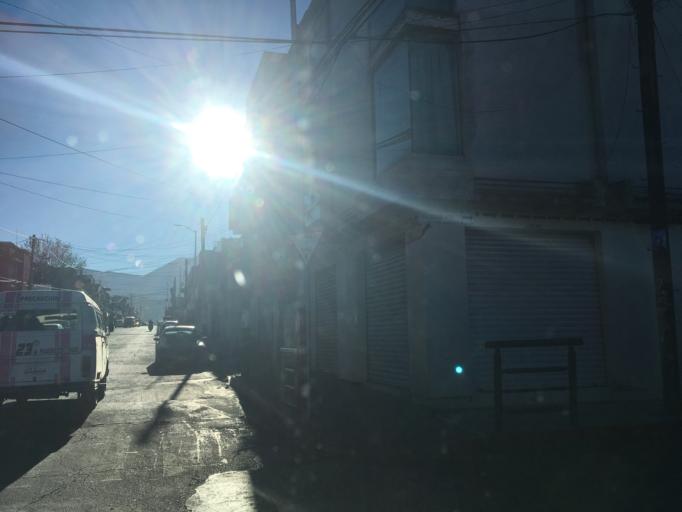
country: MX
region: Michoacan
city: Heroica Zitacuaro
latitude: 19.4400
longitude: -100.3525
